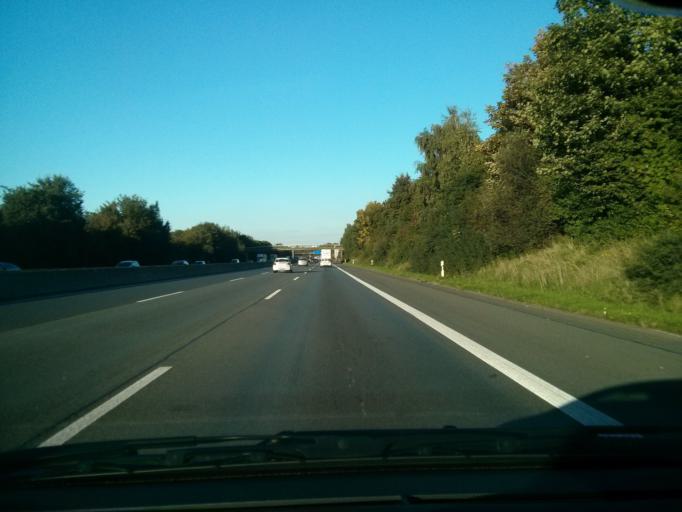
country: DE
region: North Rhine-Westphalia
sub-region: Regierungsbezirk Arnsberg
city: Holzwickede
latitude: 51.4984
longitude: 7.6403
